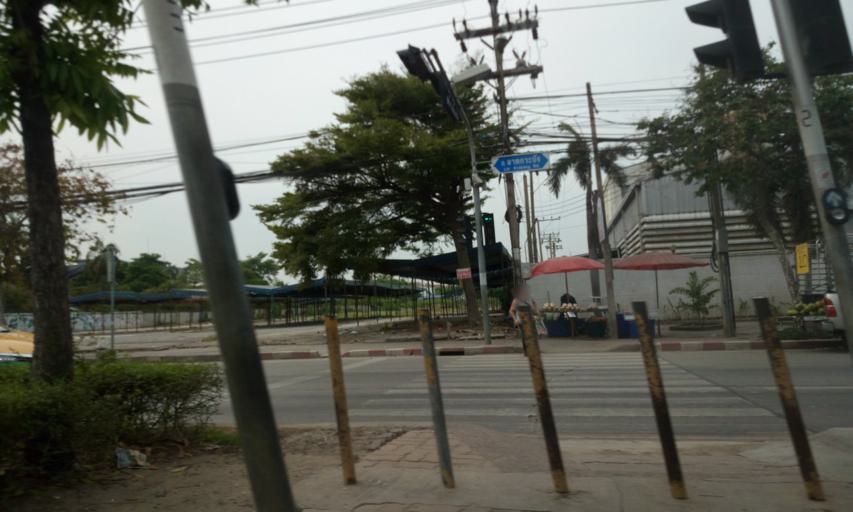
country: TH
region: Bangkok
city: Saphan Sung
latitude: 13.7222
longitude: 100.7178
